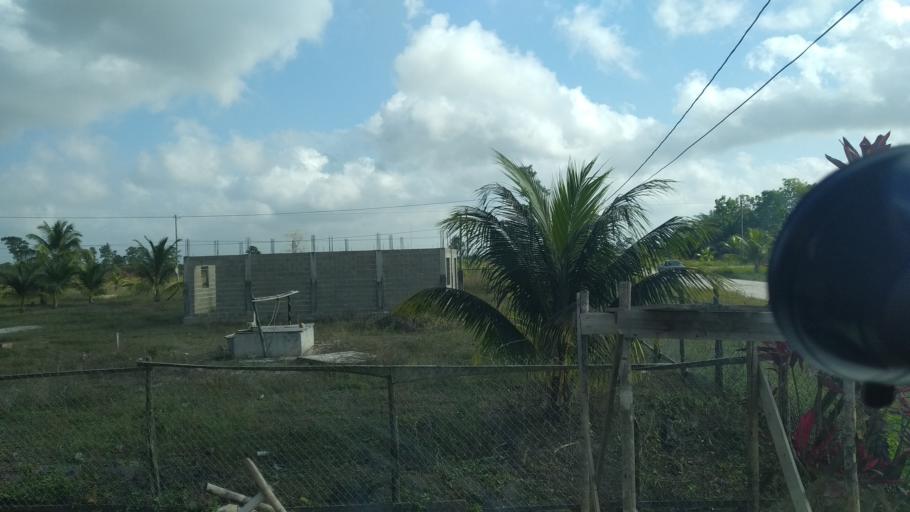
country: BZ
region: Stann Creek
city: Placencia
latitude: 16.5123
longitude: -88.5440
